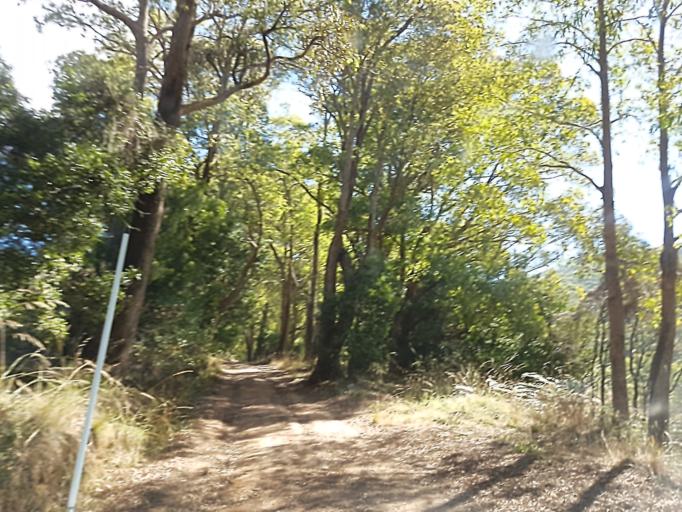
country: AU
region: Victoria
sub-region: Alpine
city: Mount Beauty
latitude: -36.8748
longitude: 147.0548
